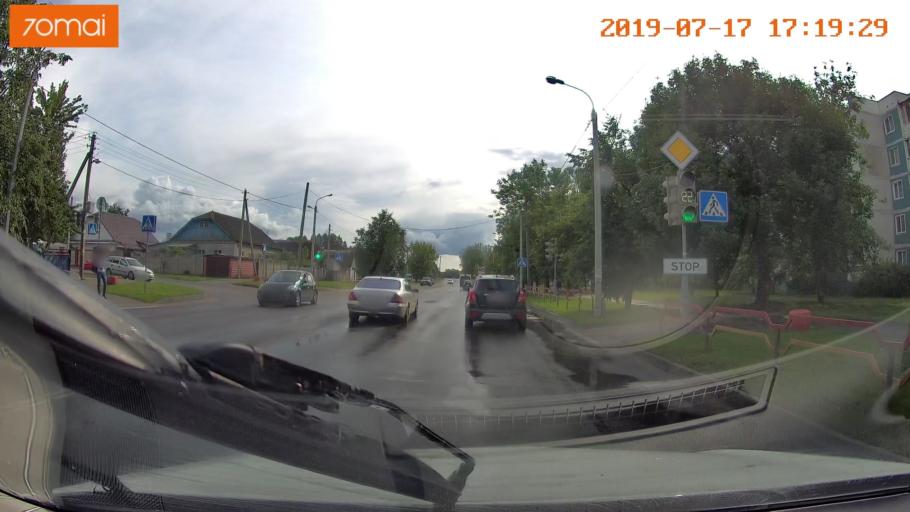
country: BY
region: Mogilev
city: Babruysk
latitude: 53.1574
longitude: 29.1924
